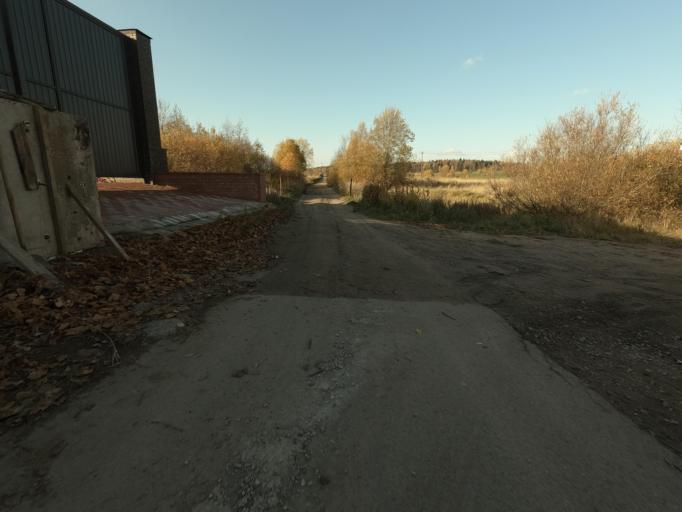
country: RU
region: Leningrad
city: Luppolovo
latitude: 60.1389
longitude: 30.2542
